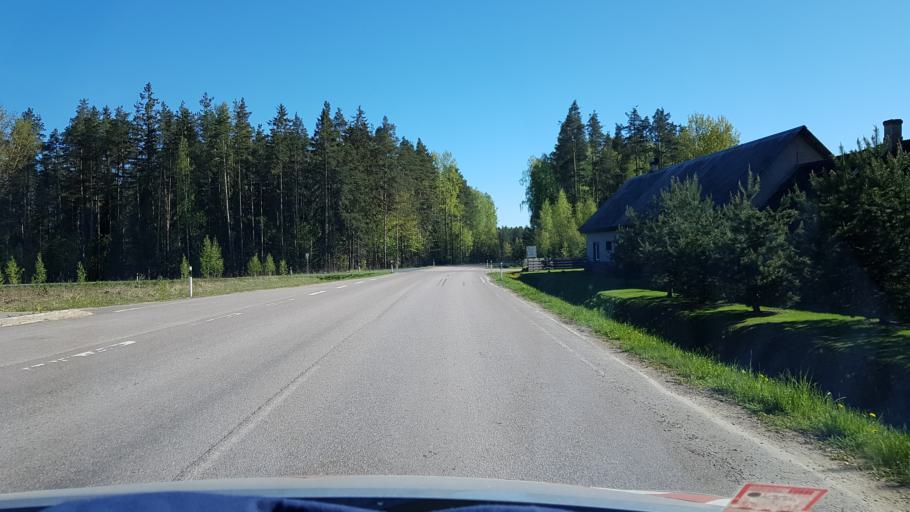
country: EE
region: Polvamaa
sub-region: Polva linn
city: Polva
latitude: 58.0971
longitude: 27.0953
